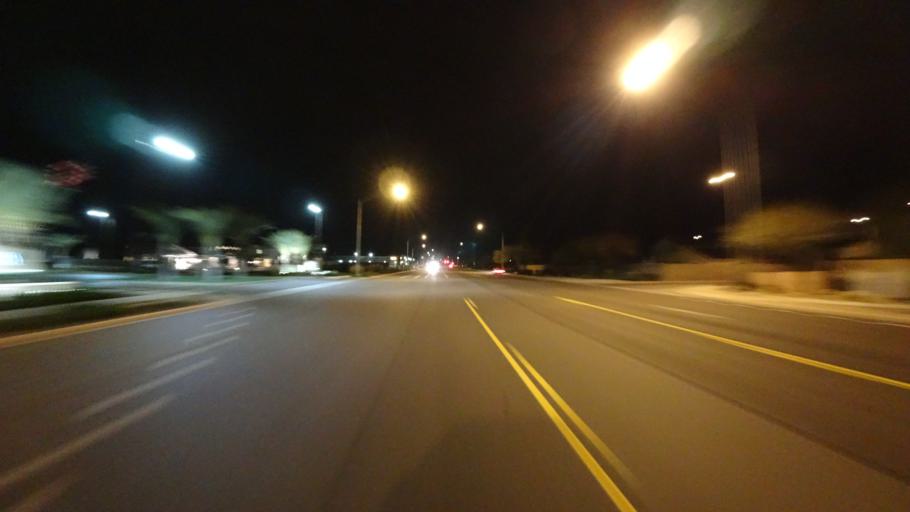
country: US
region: Arizona
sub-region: Pinal County
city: Apache Junction
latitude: 33.3644
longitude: -111.6065
